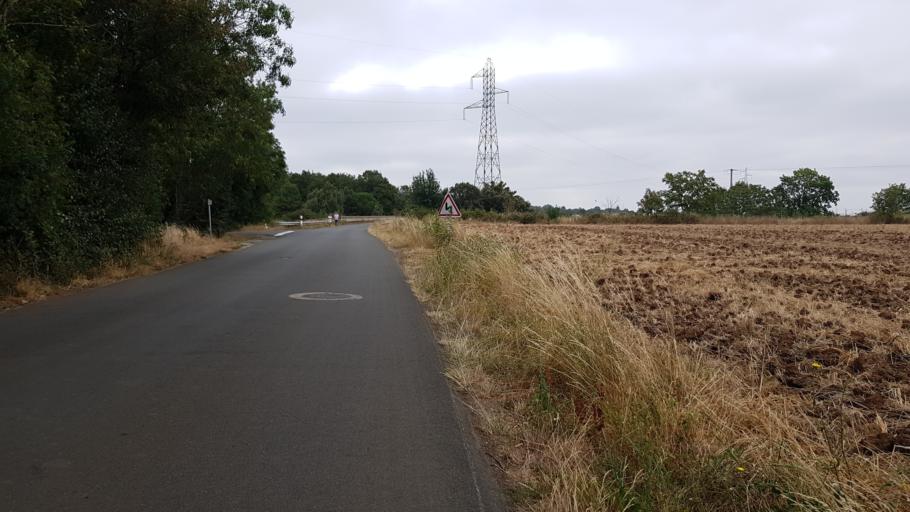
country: FR
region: Poitou-Charentes
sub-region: Departement des Deux-Sevres
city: Vouille
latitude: 46.3262
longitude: -0.3393
